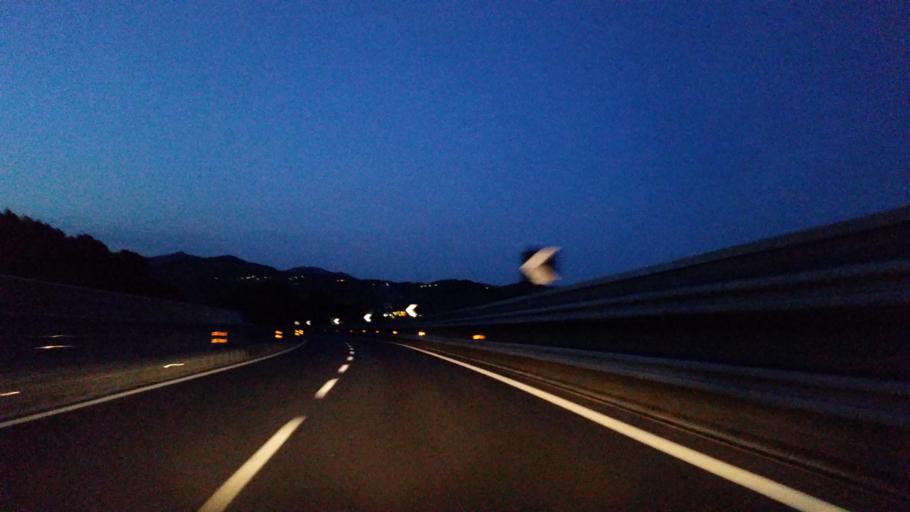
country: IT
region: Liguria
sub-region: Provincia di Savona
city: Andora
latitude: 43.9516
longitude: 8.1334
